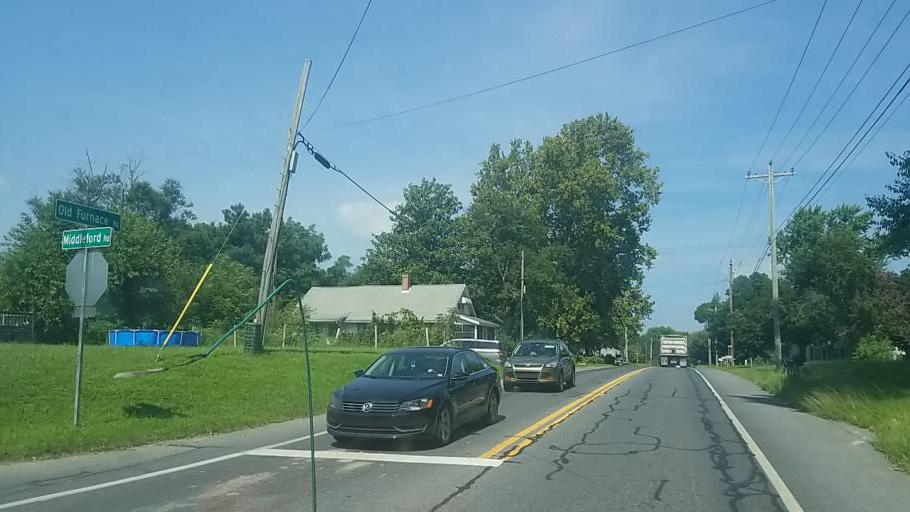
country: US
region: Delaware
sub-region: Sussex County
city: Seaford
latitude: 38.6667
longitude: -75.5675
